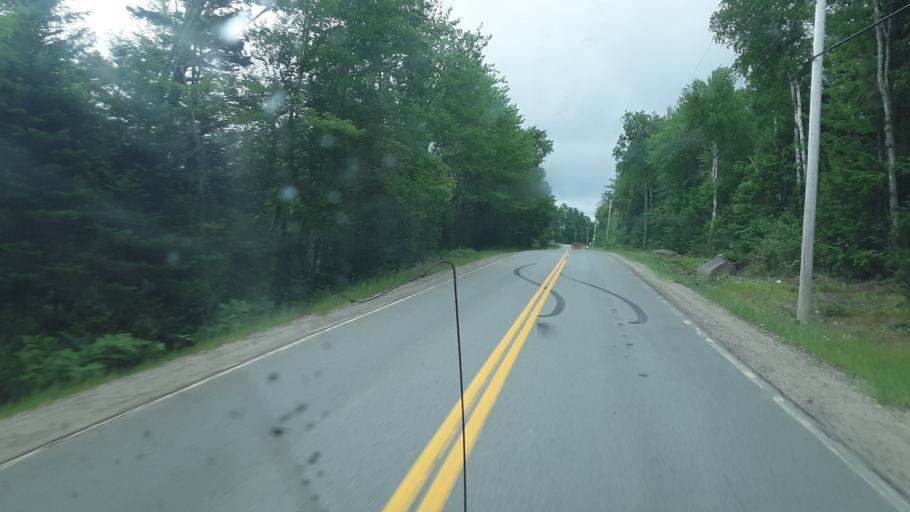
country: US
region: Maine
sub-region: Penobscot County
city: Millinocket
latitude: 45.6823
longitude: -68.7653
